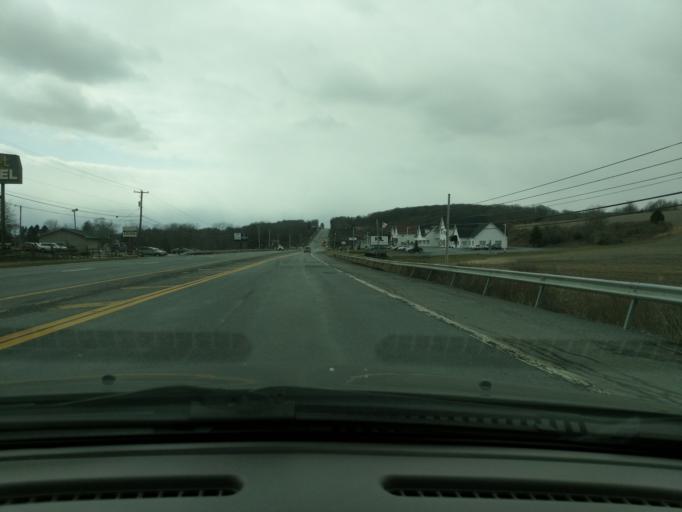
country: US
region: Pennsylvania
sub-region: Schuylkill County
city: Orwigsburg
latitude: 40.6411
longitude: -76.1005
